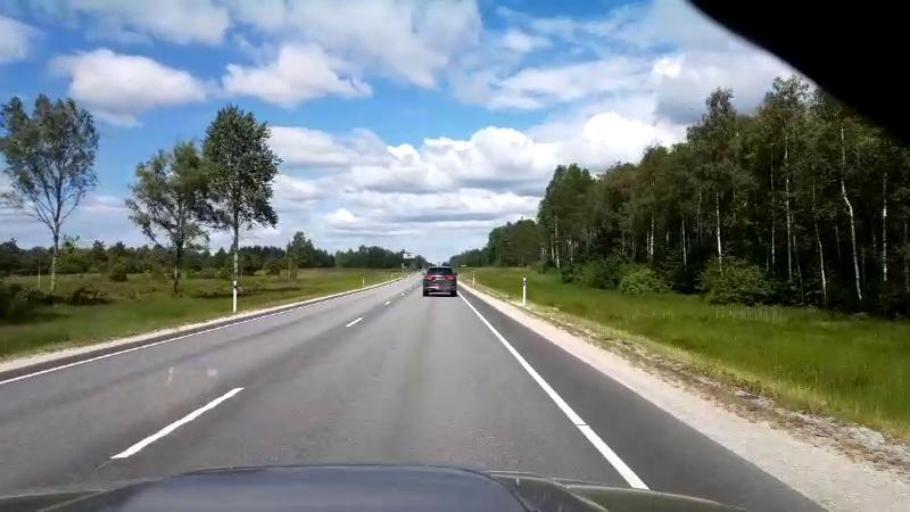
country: EE
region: Harju
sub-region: Nissi vald
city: Riisipere
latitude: 59.0831
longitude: 24.4584
